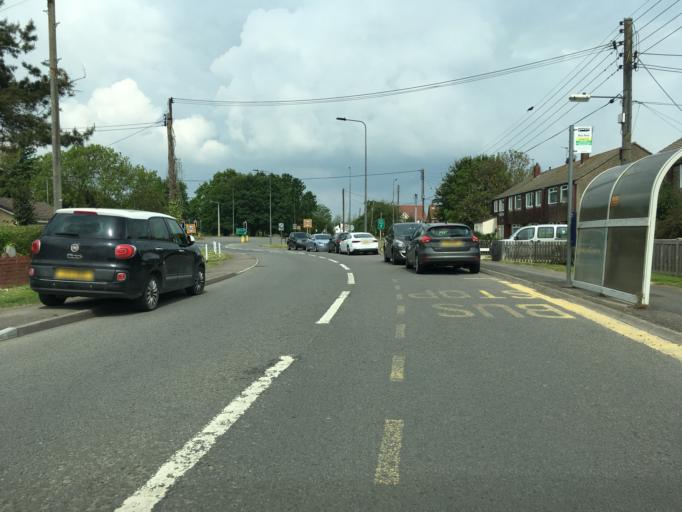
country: GB
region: England
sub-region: South Gloucestershire
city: Severn Beach
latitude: 51.5643
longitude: -2.6467
